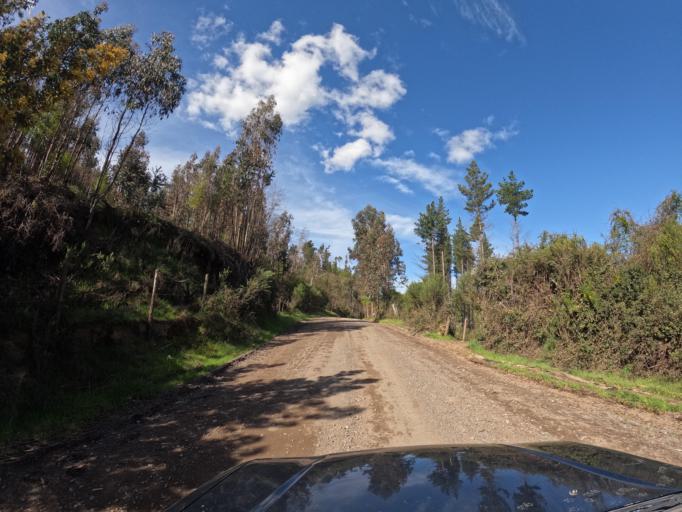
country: CL
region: Biobio
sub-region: Provincia de Concepcion
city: Chiguayante
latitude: -37.0678
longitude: -72.8499
